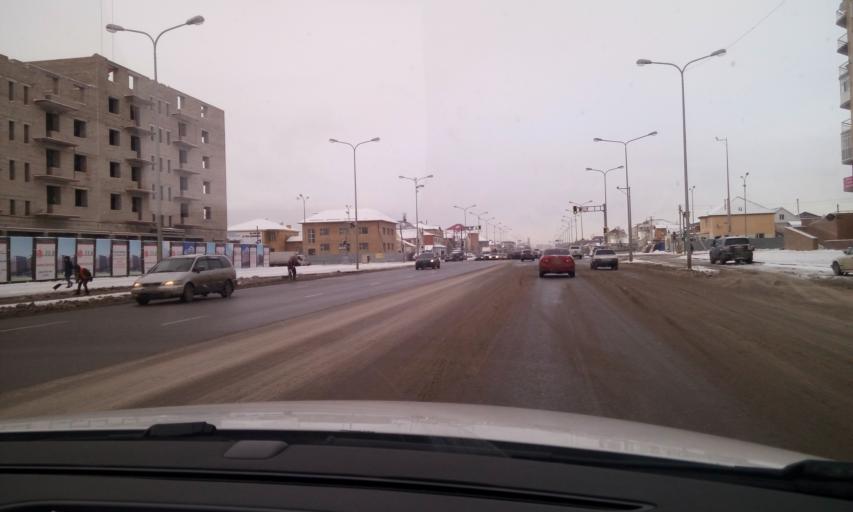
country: KZ
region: Astana Qalasy
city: Astana
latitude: 51.1305
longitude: 71.4963
